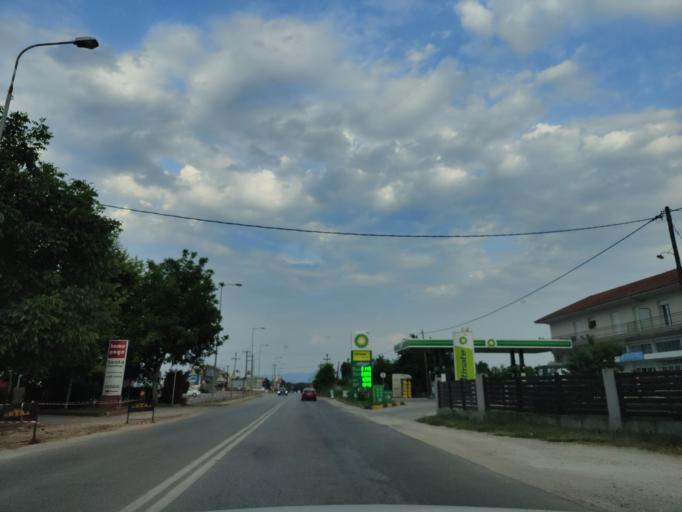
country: GR
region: East Macedonia and Thrace
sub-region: Nomos Dramas
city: Xiropotamos
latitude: 41.1563
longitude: 24.1057
